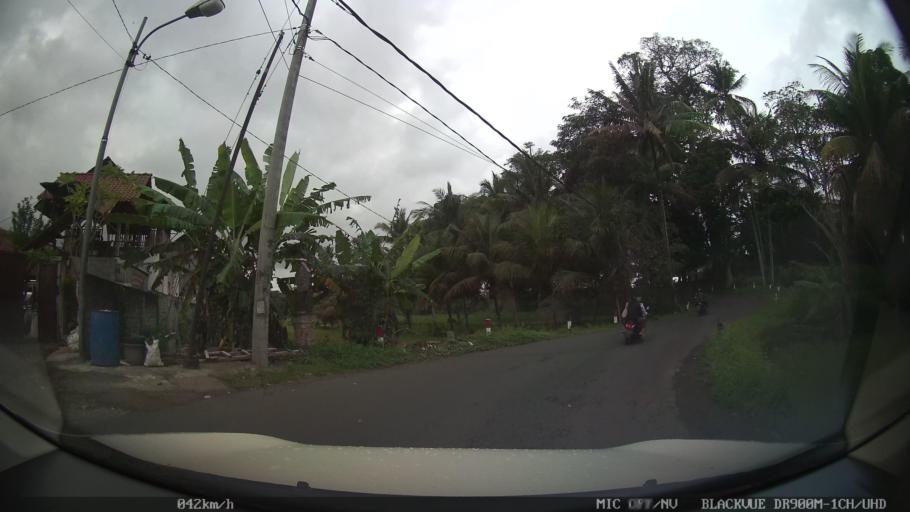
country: ID
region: Bali
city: Banjar Cemenggon
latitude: -8.5503
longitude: 115.1944
